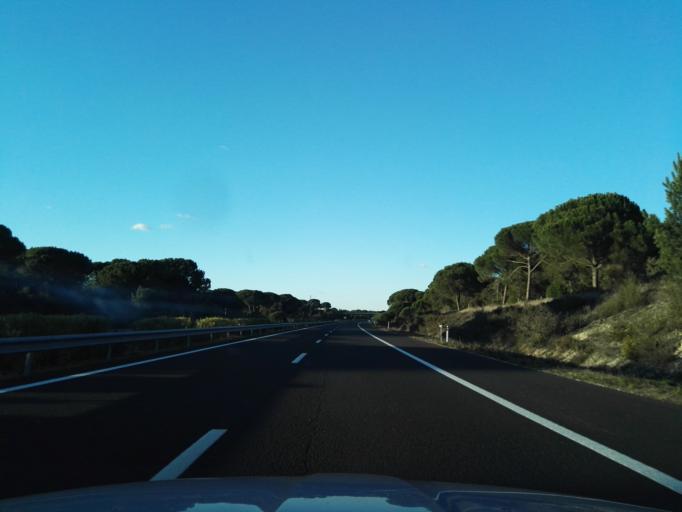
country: PT
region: Santarem
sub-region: Benavente
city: Poceirao
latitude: 38.7387
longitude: -8.6798
